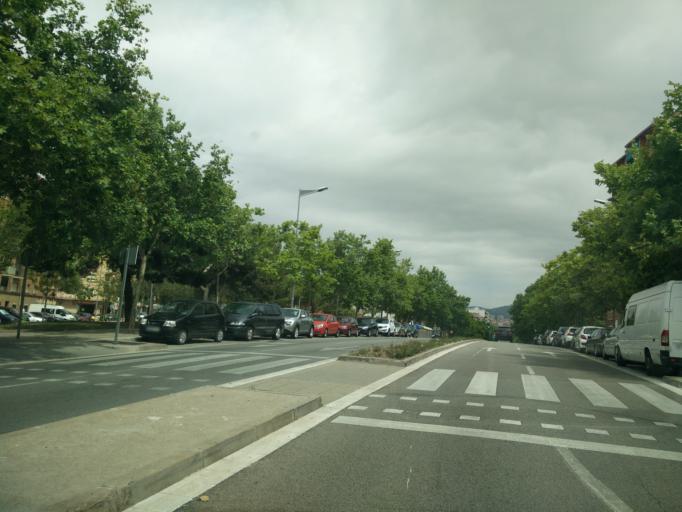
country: ES
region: Catalonia
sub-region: Provincia de Barcelona
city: Terrassa
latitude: 41.5522
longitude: 2.0263
